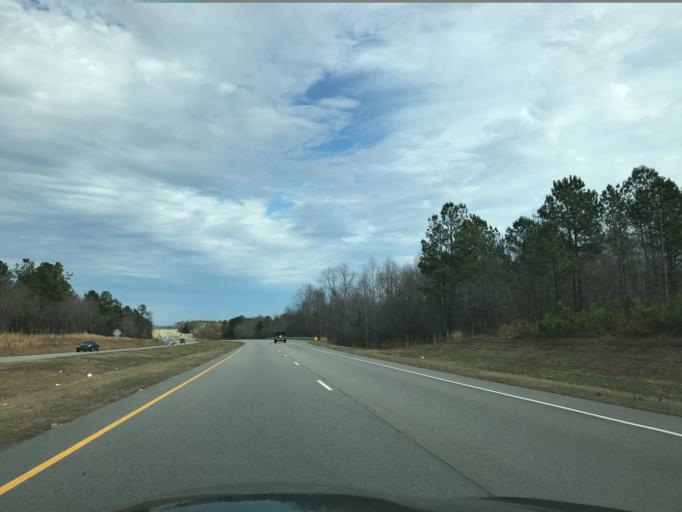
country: US
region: North Carolina
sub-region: Wake County
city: Rolesville
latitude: 35.9169
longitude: -78.4460
